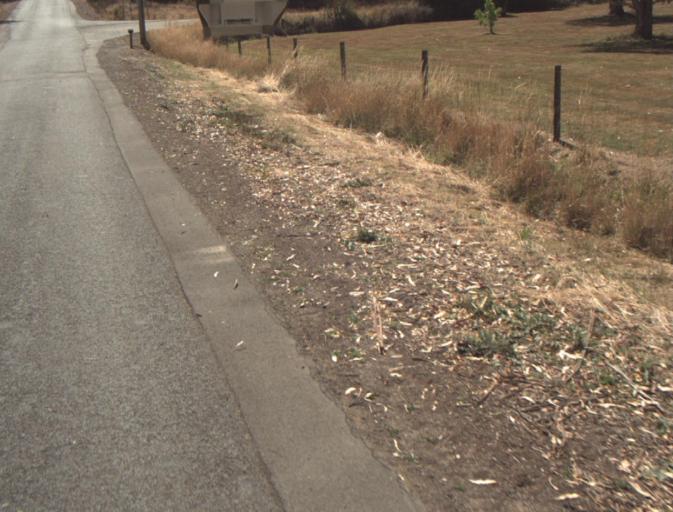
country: AU
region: Tasmania
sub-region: Launceston
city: Newstead
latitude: -41.3218
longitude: 147.3218
